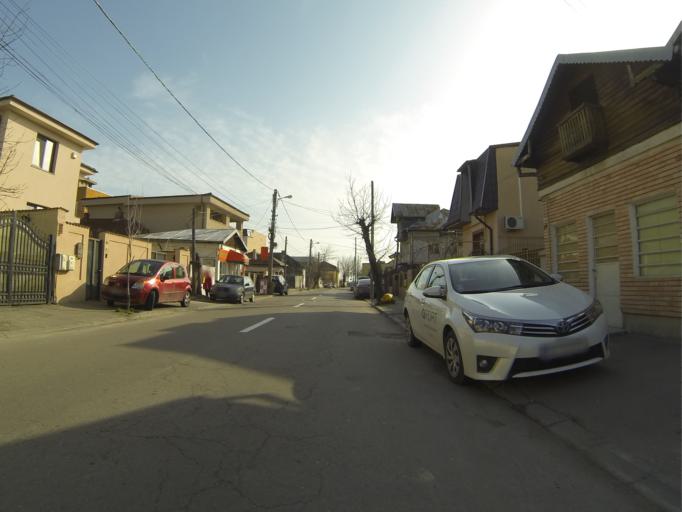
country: RO
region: Dolj
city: Craiova
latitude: 44.3110
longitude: 23.8111
